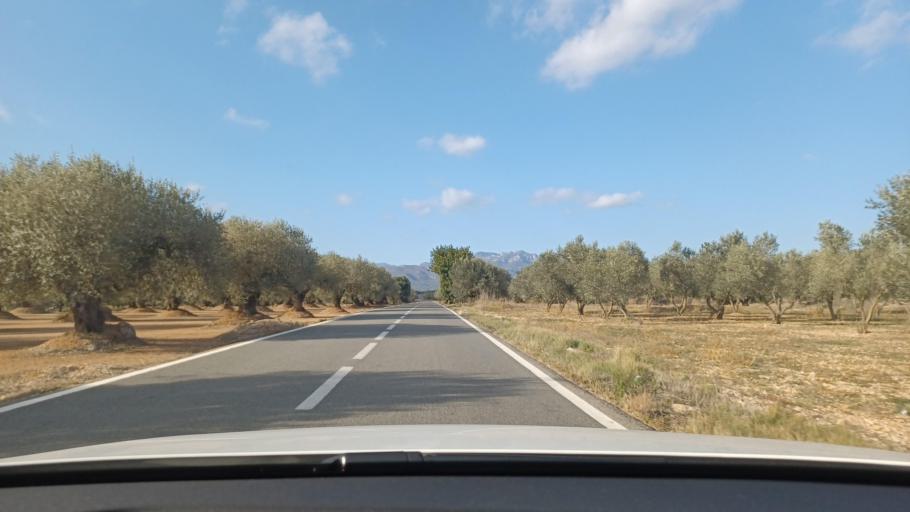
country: ES
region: Catalonia
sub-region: Provincia de Tarragona
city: Ulldecona
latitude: 40.6342
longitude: 0.3594
